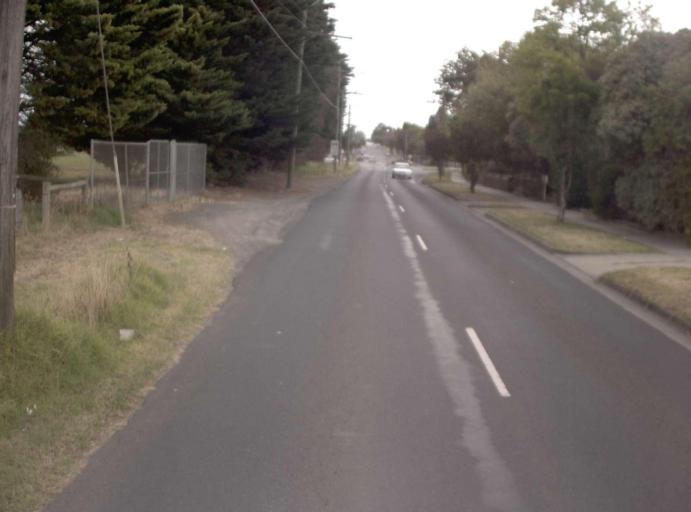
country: AU
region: Victoria
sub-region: Monash
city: Oakleigh South
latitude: -37.9422
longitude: 145.0976
